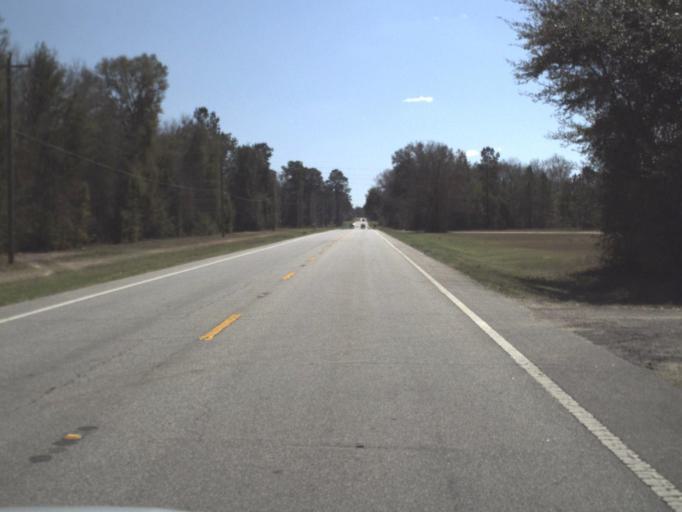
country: US
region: Florida
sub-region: Gadsden County
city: Gretna
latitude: 30.6893
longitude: -84.6218
